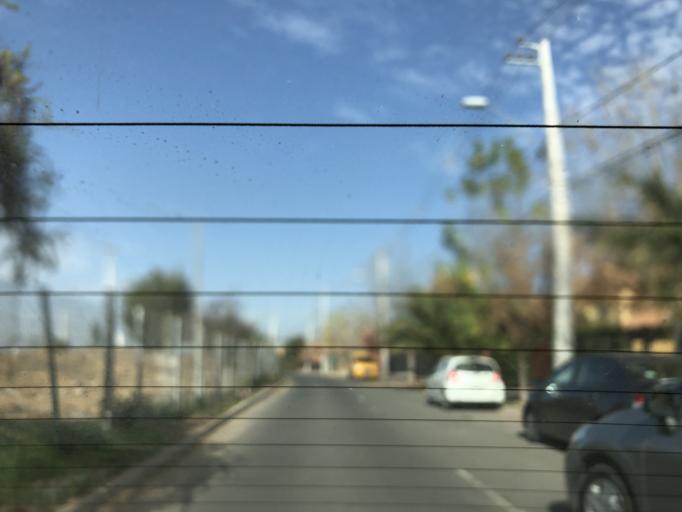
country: CL
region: Santiago Metropolitan
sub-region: Provincia de Cordillera
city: Puente Alto
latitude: -33.5908
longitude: -70.5362
